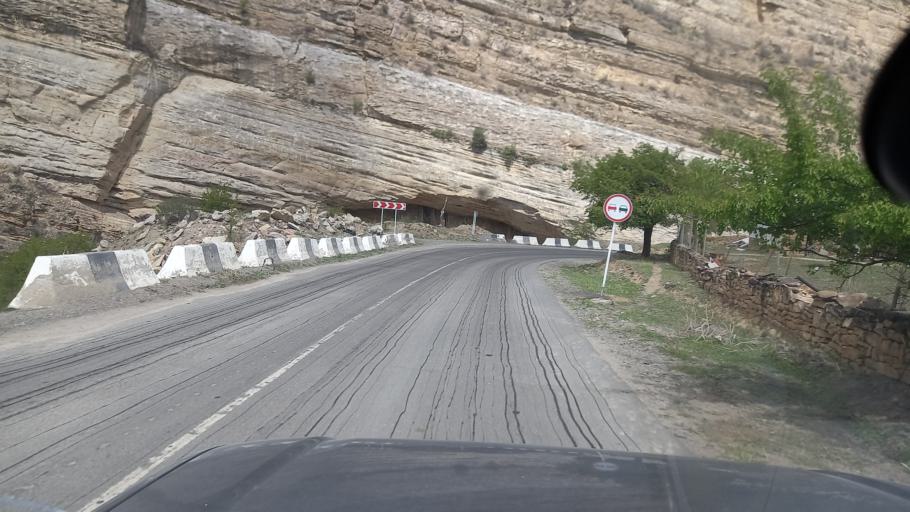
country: RU
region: Dagestan
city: Gunib
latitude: 42.3188
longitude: 46.9224
